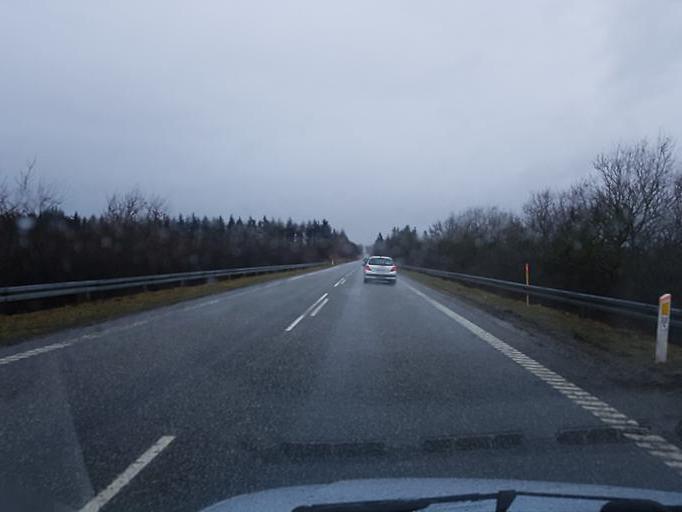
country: DK
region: Central Jutland
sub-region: Ringkobing-Skjern Kommune
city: Videbaek
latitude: 56.1574
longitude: 8.5270
